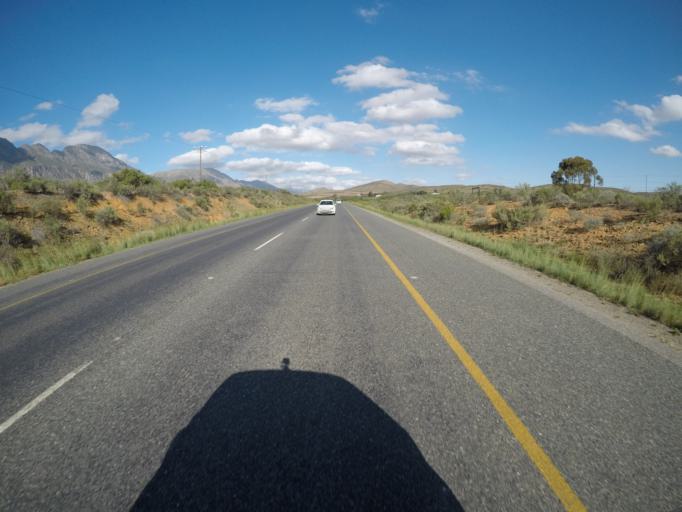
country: ZA
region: Western Cape
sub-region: Cape Winelands District Municipality
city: Ashton
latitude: -33.8570
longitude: 20.1094
